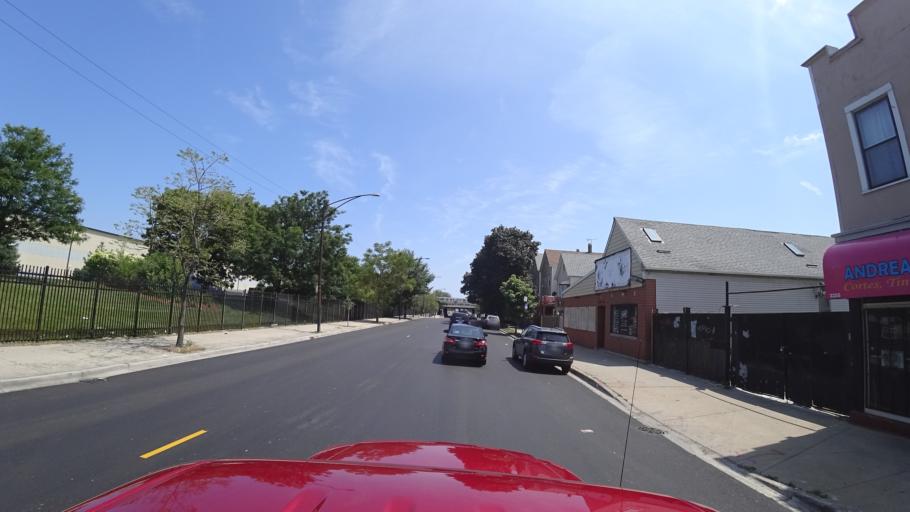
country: US
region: Illinois
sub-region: Cook County
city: Chicago
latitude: 41.8084
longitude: -87.6819
